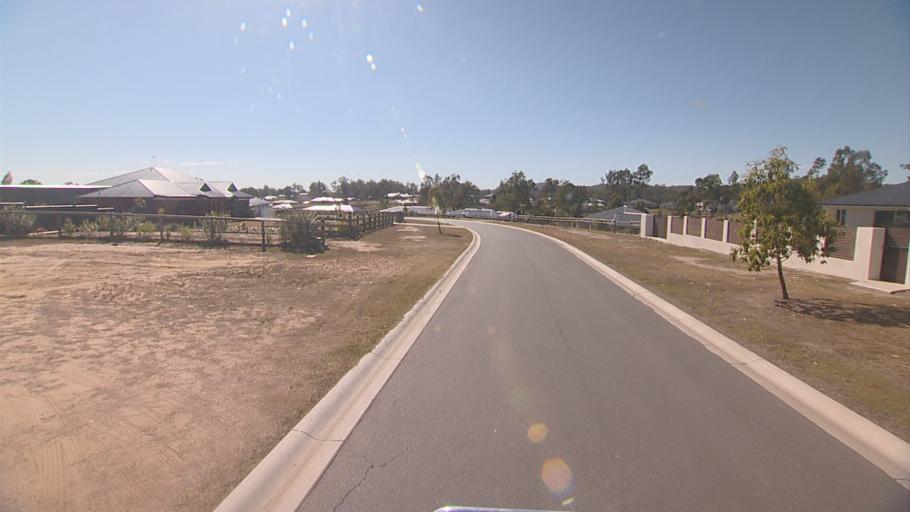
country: AU
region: Queensland
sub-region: Logan
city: Cedar Vale
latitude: -27.8712
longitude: 153.0453
